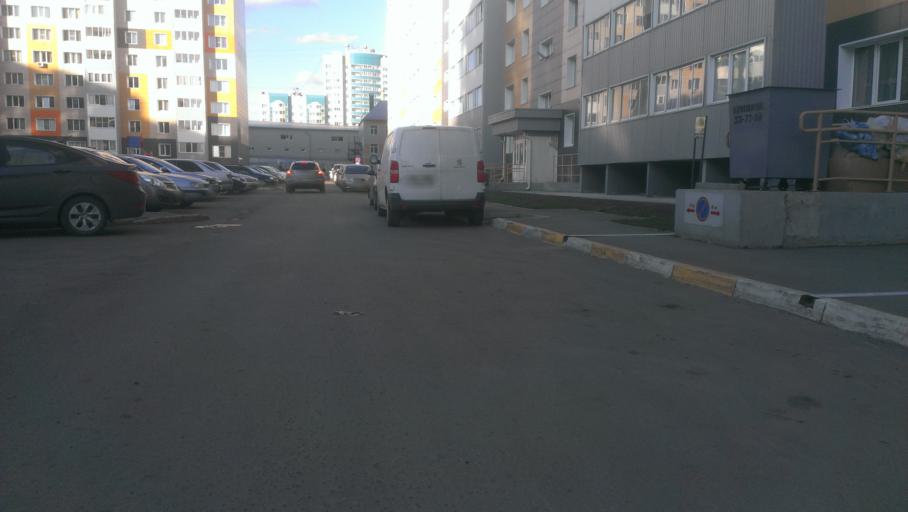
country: RU
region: Altai Krai
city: Novosilikatnyy
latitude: 53.3382
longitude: 83.6601
